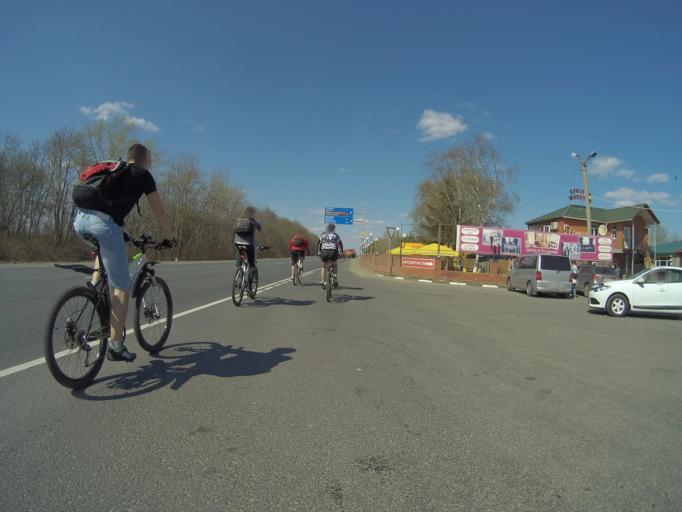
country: RU
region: Vladimir
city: Suzdal'
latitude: 56.3824
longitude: 40.4558
